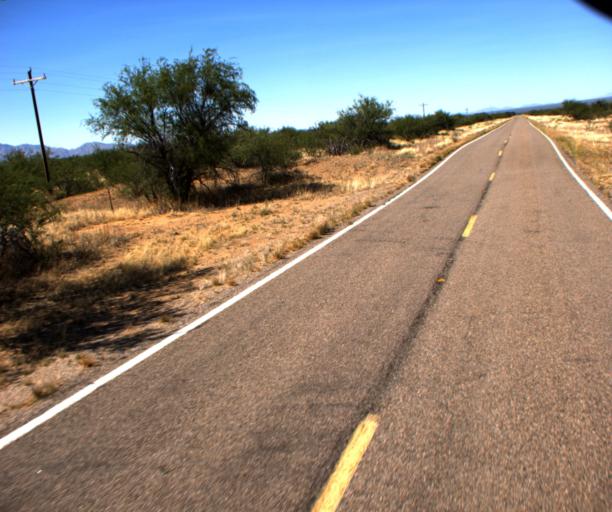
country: US
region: Arizona
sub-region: Pima County
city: Three Points
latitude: 31.7845
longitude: -111.4582
